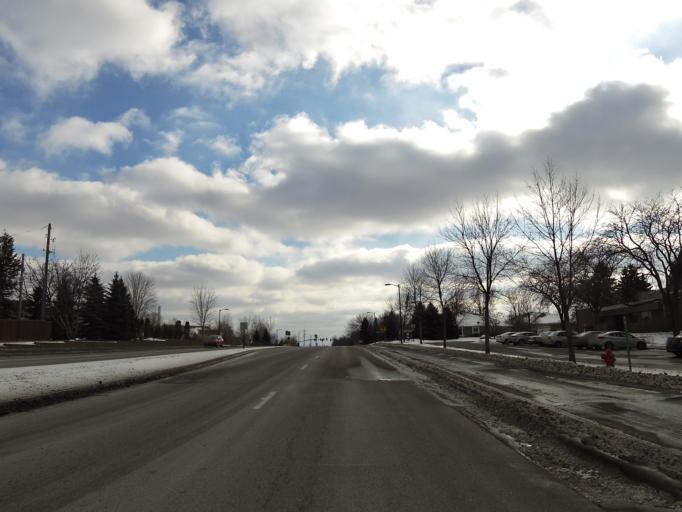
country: US
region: Minnesota
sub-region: Hennepin County
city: Eden Prairie
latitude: 44.8414
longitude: -93.4808
